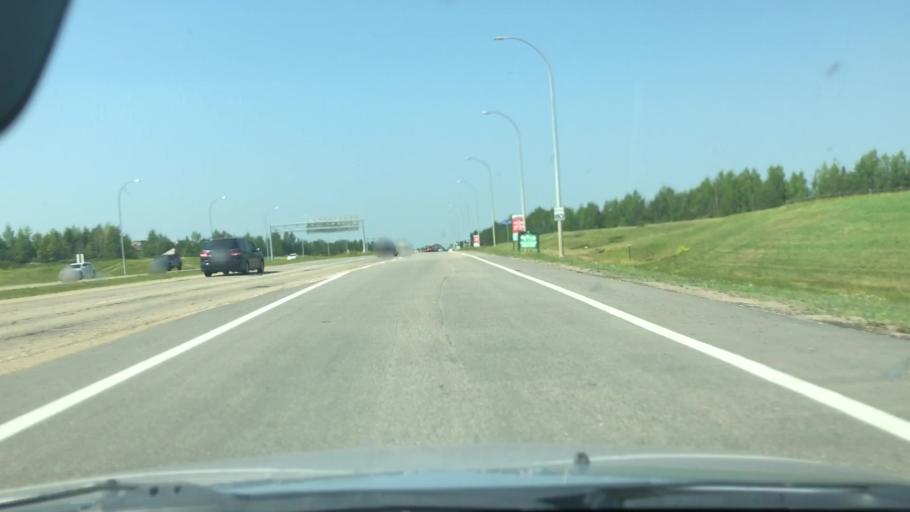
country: CA
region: Alberta
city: St. Albert
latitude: 53.5126
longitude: -113.6652
